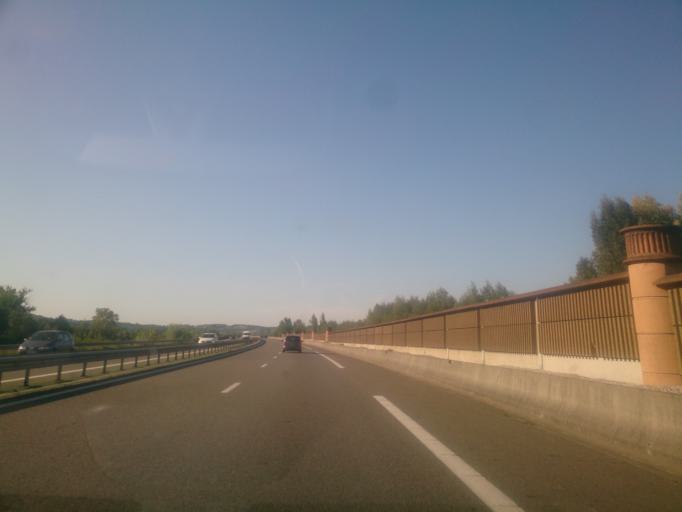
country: FR
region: Midi-Pyrenees
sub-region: Departement du Tarn-et-Garonne
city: Albias
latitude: 44.0677
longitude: 1.4229
